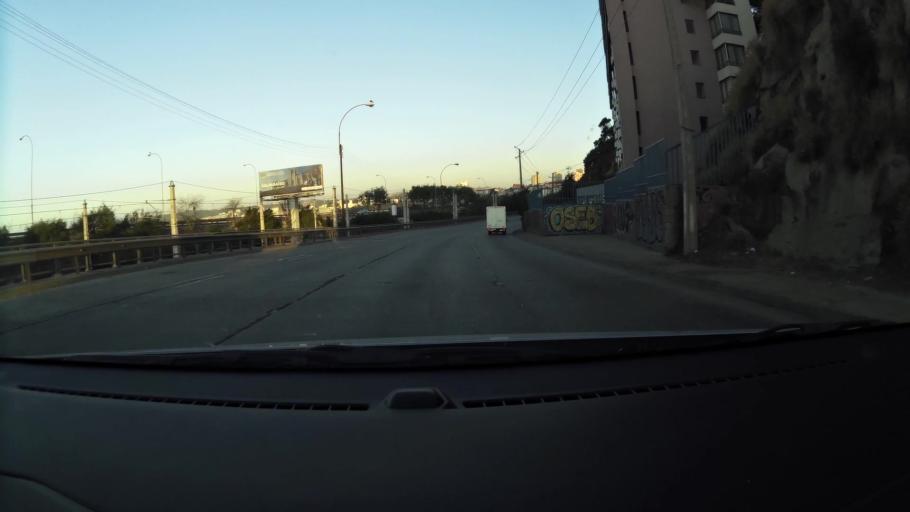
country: CL
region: Valparaiso
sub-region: Provincia de Valparaiso
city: Vina del Mar
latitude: -33.0260
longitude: -71.5837
